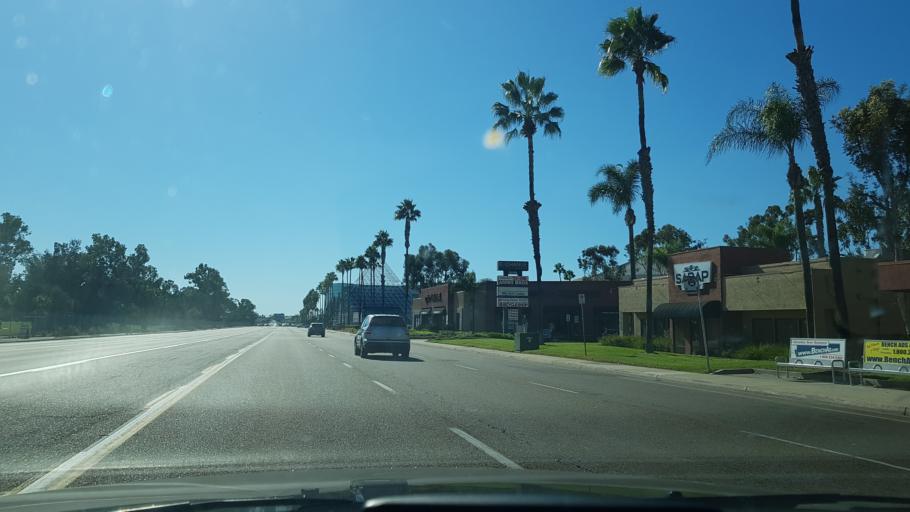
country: US
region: California
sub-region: San Diego County
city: Fairbanks Ranch
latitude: 32.8846
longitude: -117.1518
